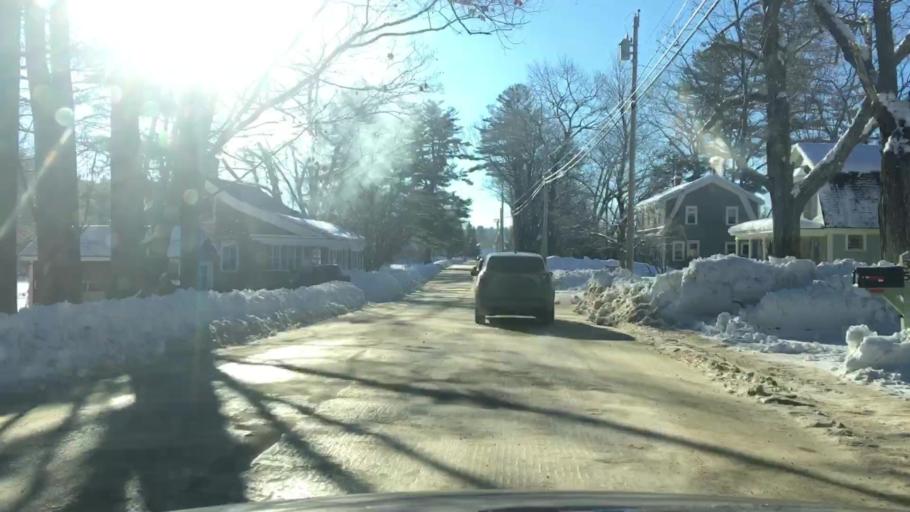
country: US
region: Maine
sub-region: Oxford County
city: West Paris
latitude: 44.3855
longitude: -70.6440
